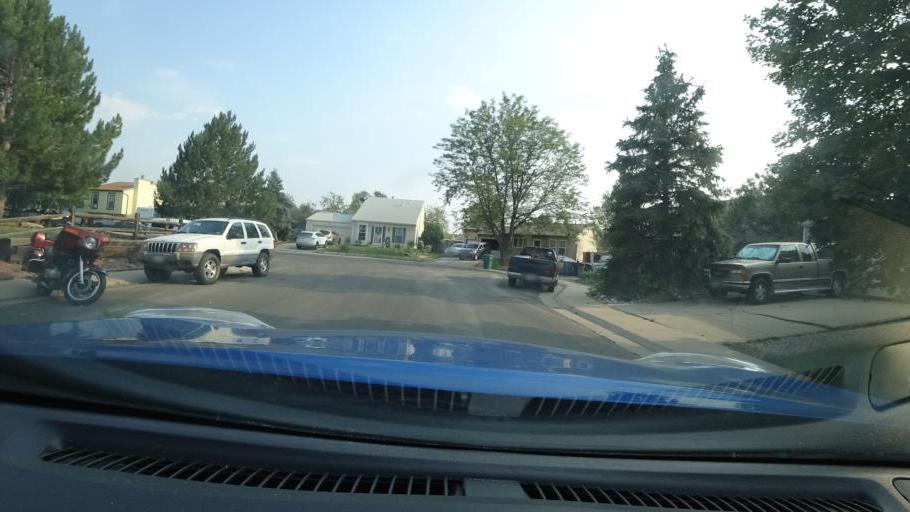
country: US
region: Colorado
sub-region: Adams County
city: Aurora
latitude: 39.7466
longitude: -104.7644
